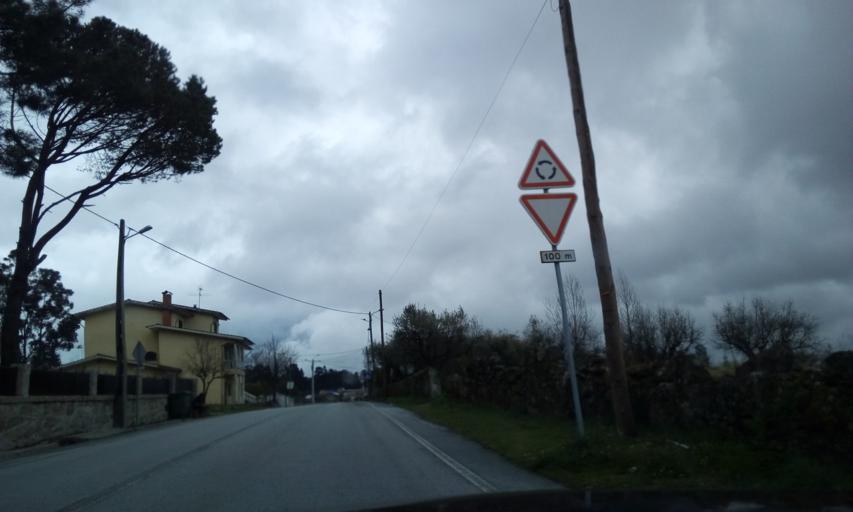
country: PT
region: Viseu
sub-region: Mangualde
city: Mangualde
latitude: 40.5978
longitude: -7.8164
